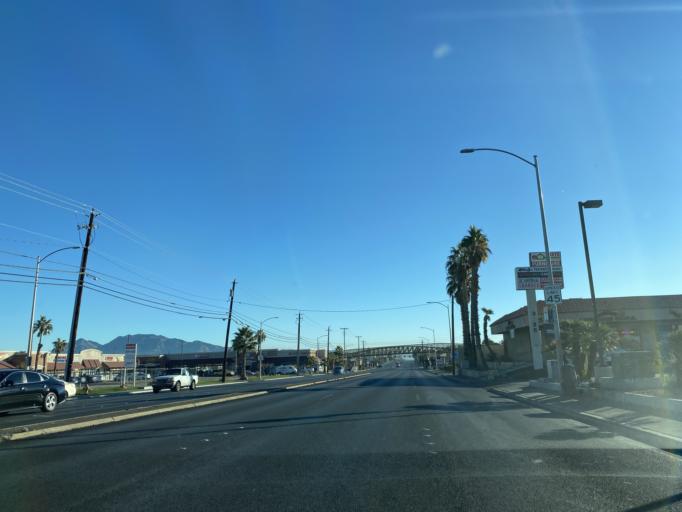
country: US
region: Nevada
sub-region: Clark County
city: Winchester
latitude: 36.1297
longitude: -115.1094
